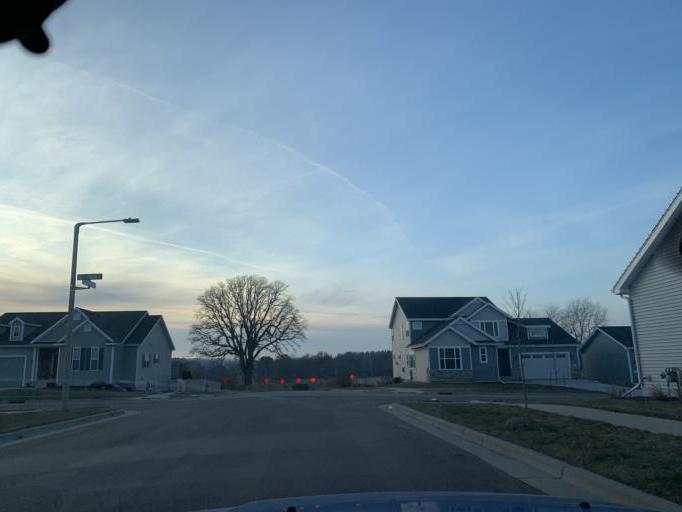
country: US
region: Wisconsin
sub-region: Dane County
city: Middleton
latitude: 43.0573
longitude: -89.5659
